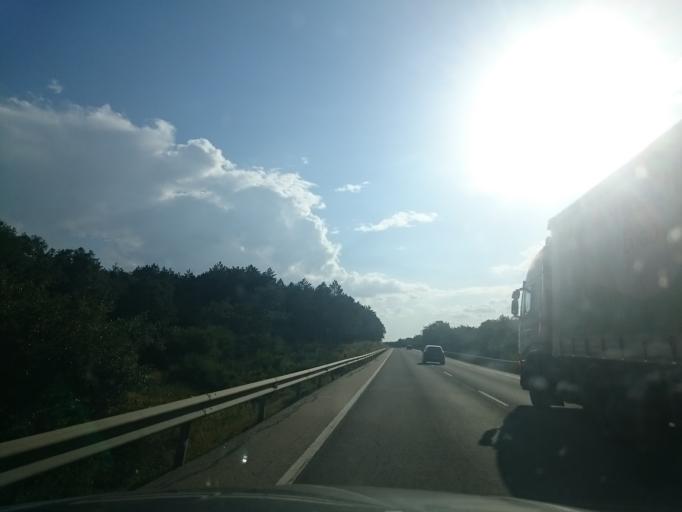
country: ES
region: Castille and Leon
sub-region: Provincia de Burgos
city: Arraya de Oca
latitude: 42.3631
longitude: -3.3743
